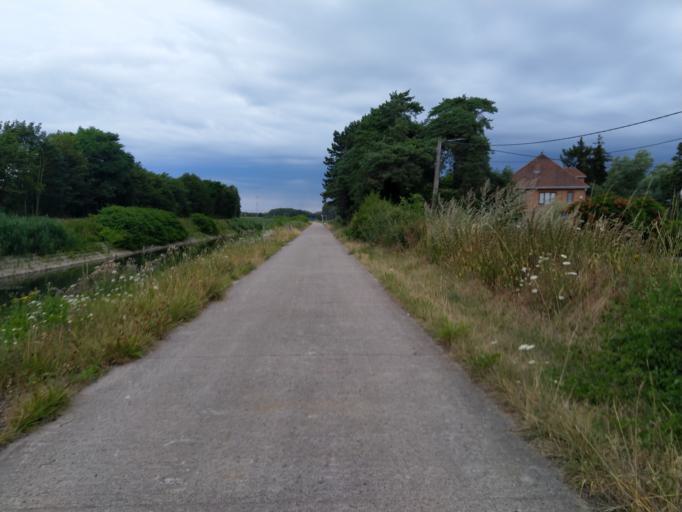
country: BE
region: Wallonia
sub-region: Province du Hainaut
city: Mons
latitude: 50.4539
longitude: 3.9235
